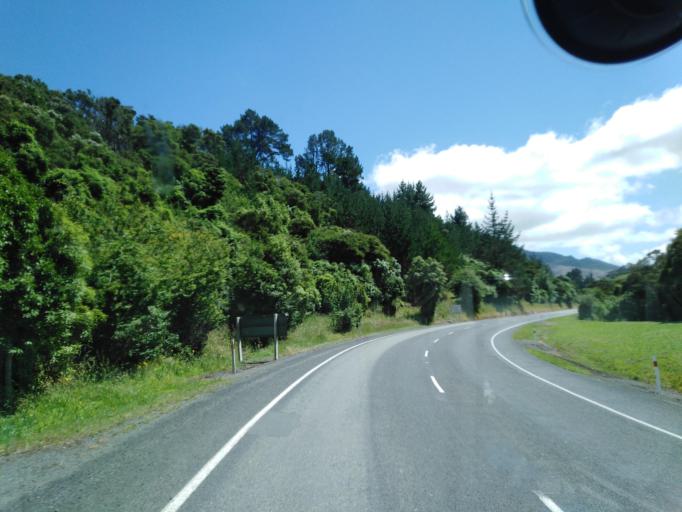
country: NZ
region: Nelson
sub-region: Nelson City
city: Nelson
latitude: -41.2255
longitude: 173.3961
